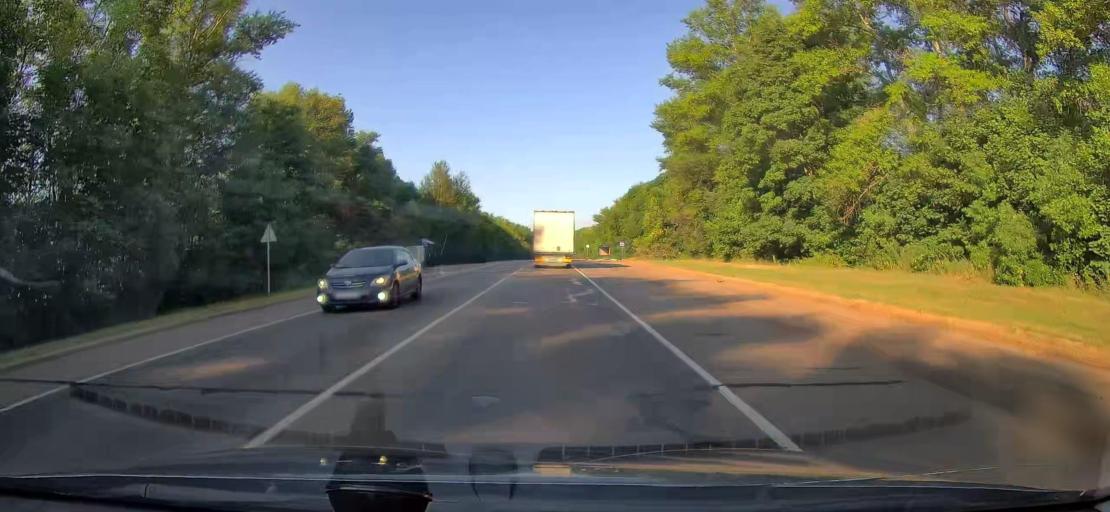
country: RU
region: Tula
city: Chern'
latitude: 53.4669
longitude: 36.9563
